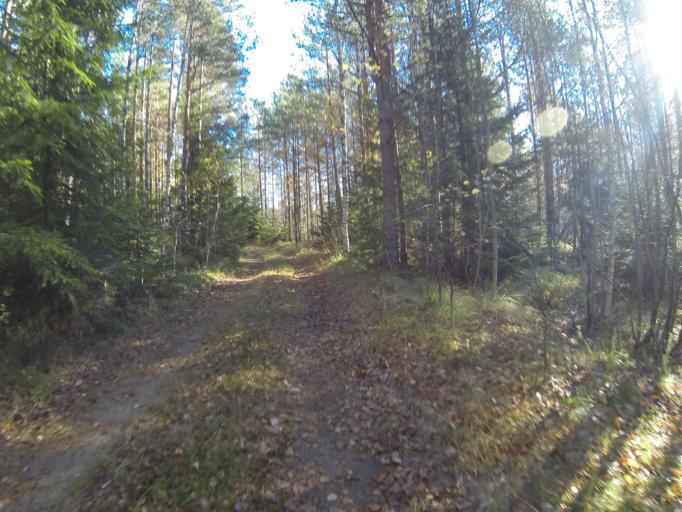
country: FI
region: Varsinais-Suomi
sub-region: Salo
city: Saerkisalo
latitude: 60.2083
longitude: 22.9494
